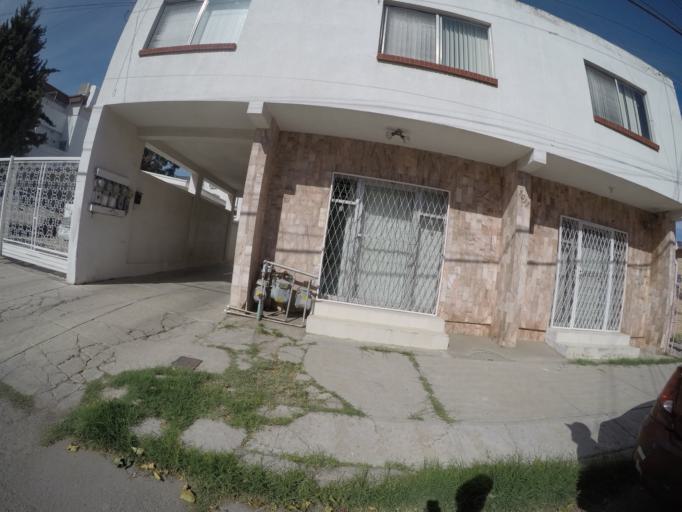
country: MX
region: Chihuahua
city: Ciudad Juarez
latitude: 31.7350
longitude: -106.4399
